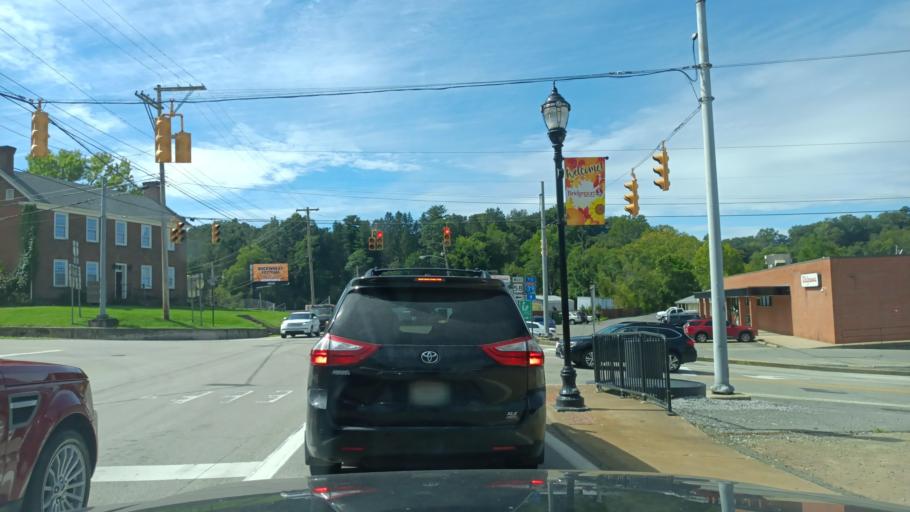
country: US
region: West Virginia
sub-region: Harrison County
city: Bridgeport
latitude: 39.2833
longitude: -80.2558
